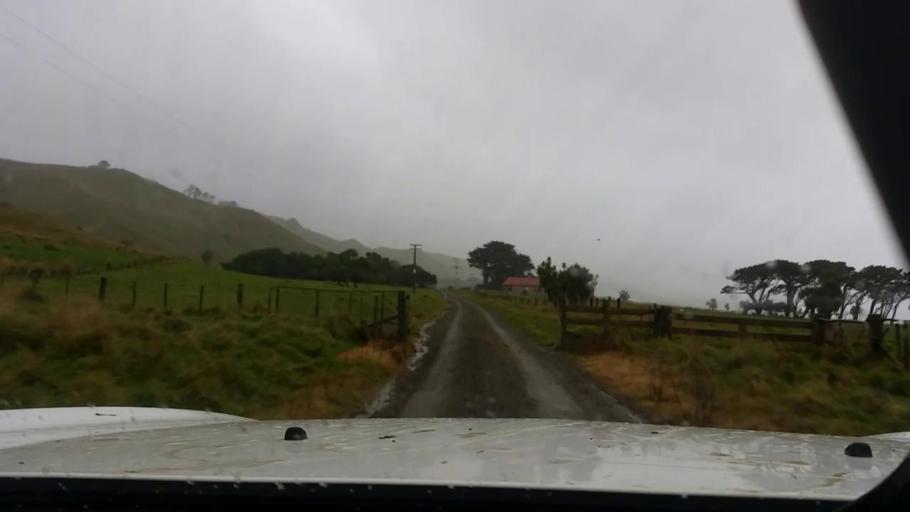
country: NZ
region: Wellington
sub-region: Masterton District
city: Masterton
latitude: -41.2636
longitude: 175.8933
